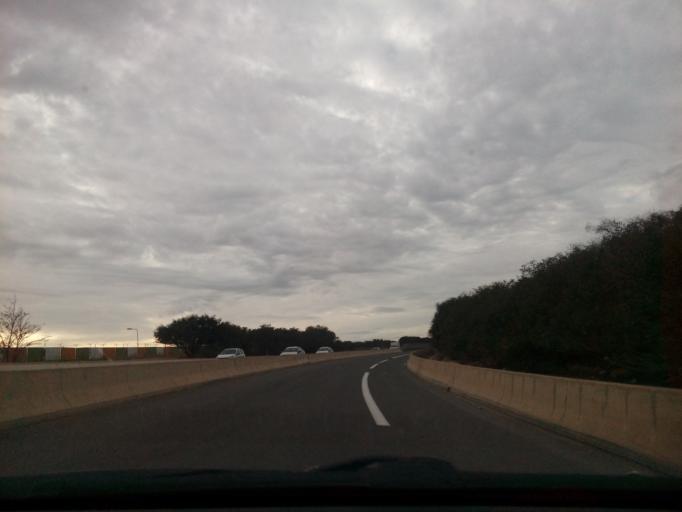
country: DZ
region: Mascara
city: Sig
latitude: 35.5421
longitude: -0.3413
